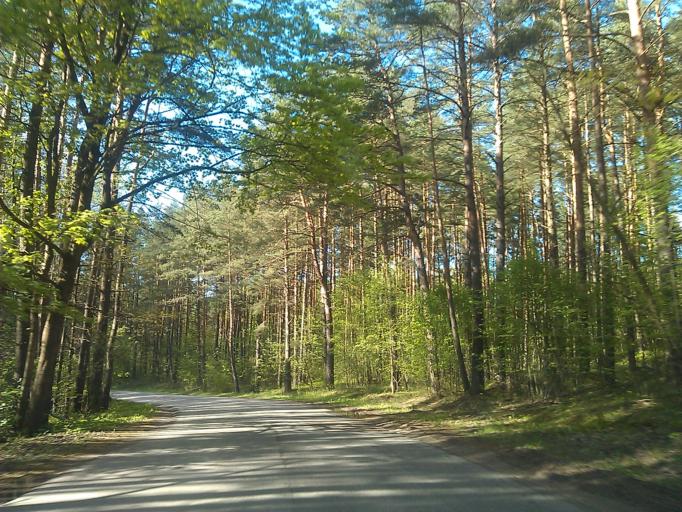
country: LV
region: Riga
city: Bergi
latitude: 57.0106
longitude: 24.2604
